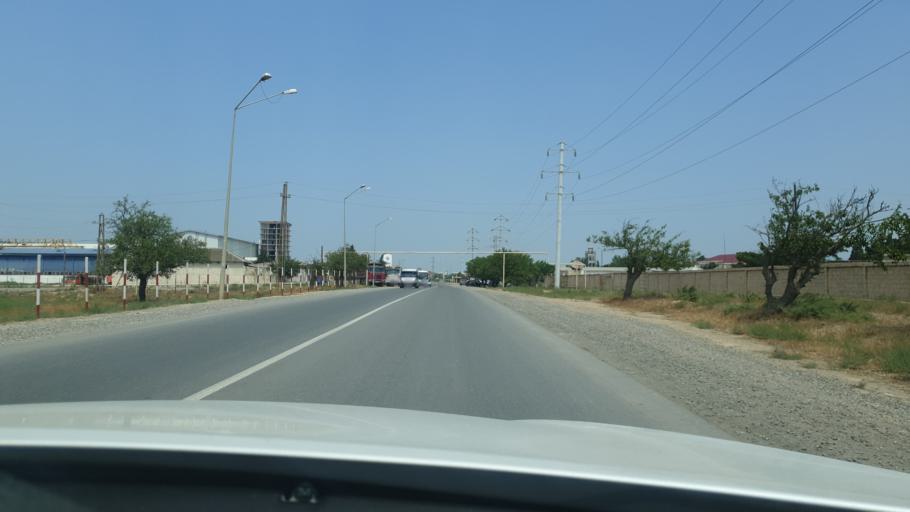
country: AZ
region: Baki
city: Qaracuxur
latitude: 40.3977
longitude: 49.9995
